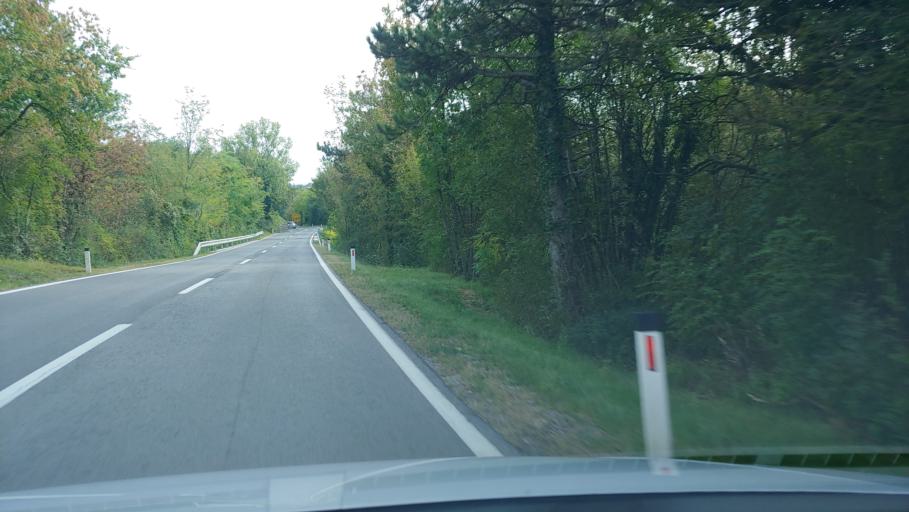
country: SI
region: Nova Gorica
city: Sempas
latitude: 45.8994
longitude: 13.7831
